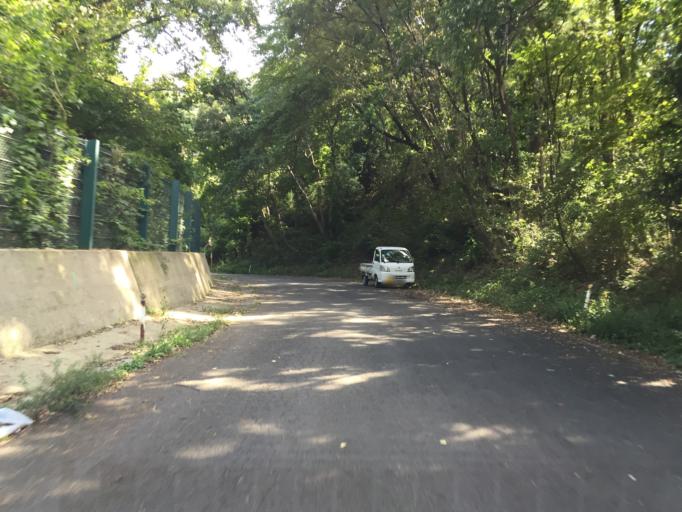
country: JP
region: Fukushima
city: Hobaramachi
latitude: 37.7725
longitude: 140.5271
